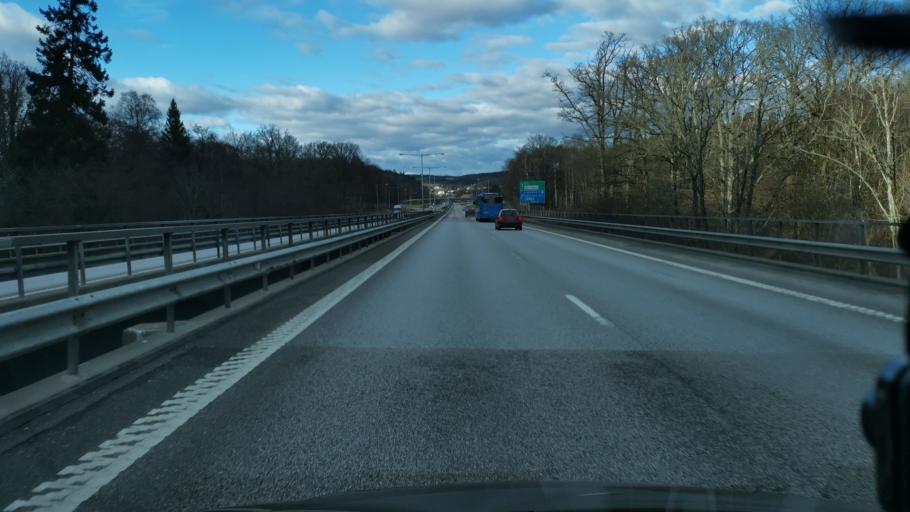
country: SE
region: Vaestra Goetaland
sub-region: Uddevalla Kommun
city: Ljungskile
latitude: 58.2074
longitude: 11.9115
